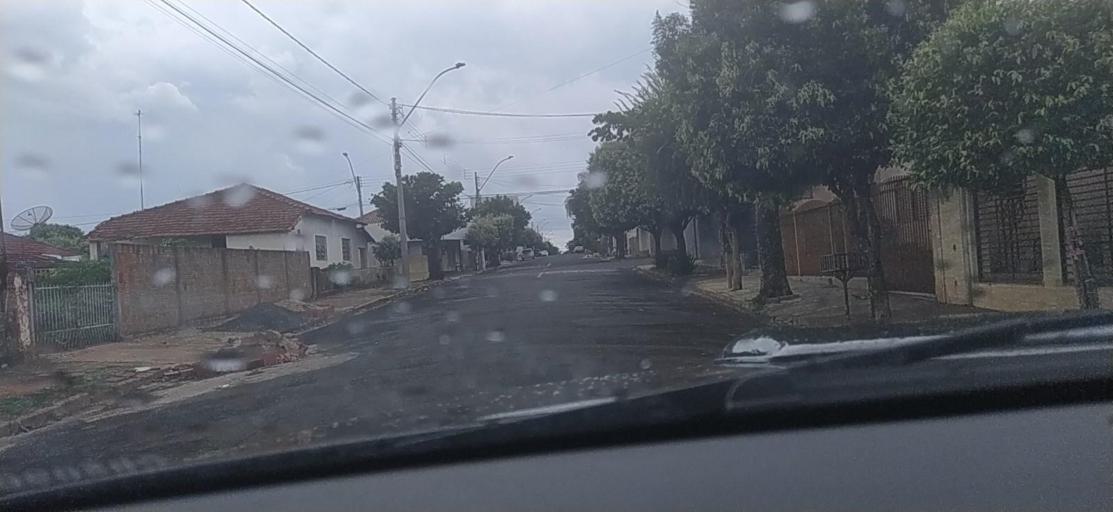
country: BR
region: Sao Paulo
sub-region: Pindorama
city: Pindorama
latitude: -21.1897
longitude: -48.9021
